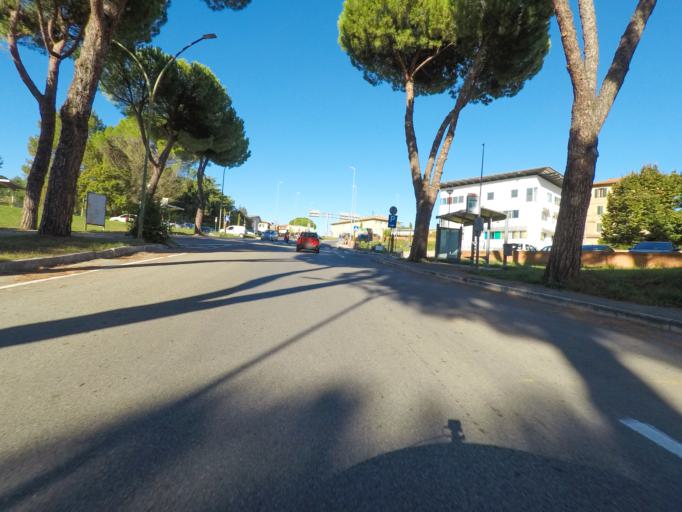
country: IT
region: Tuscany
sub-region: Provincia di Siena
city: Belverde
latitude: 43.3421
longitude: 11.3047
